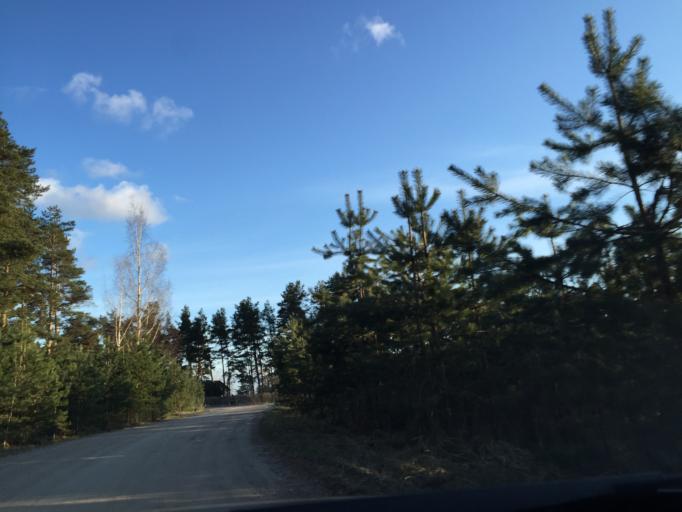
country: LV
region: Kekava
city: Kekava
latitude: 56.8629
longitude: 24.2160
